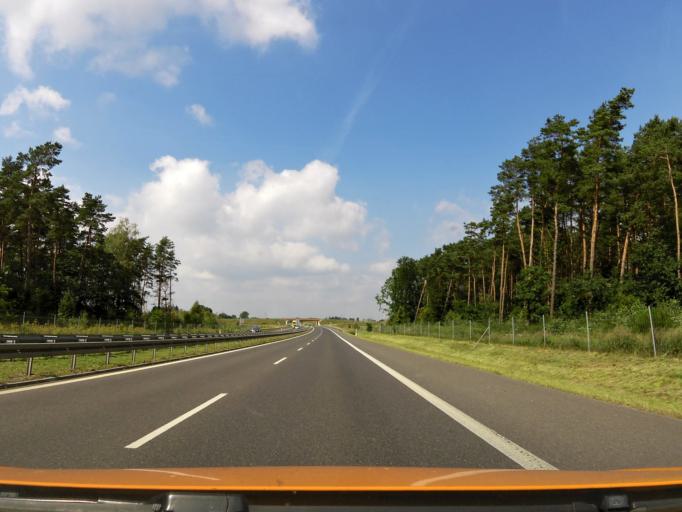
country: PL
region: West Pomeranian Voivodeship
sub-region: Powiat goleniowski
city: Nowogard
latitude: 53.6931
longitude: 15.1248
